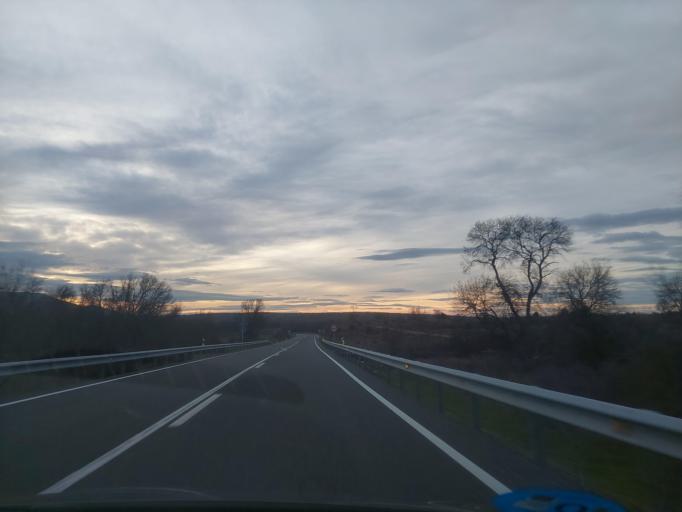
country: ES
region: Castille and Leon
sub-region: Provincia de Segovia
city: Matabuena
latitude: 41.1022
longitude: -3.7484
